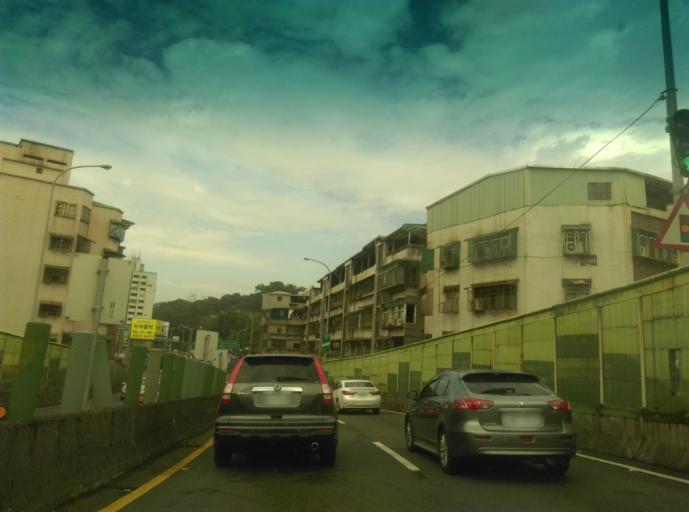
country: TW
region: Taiwan
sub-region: Keelung
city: Keelung
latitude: 25.1407
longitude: 121.7037
